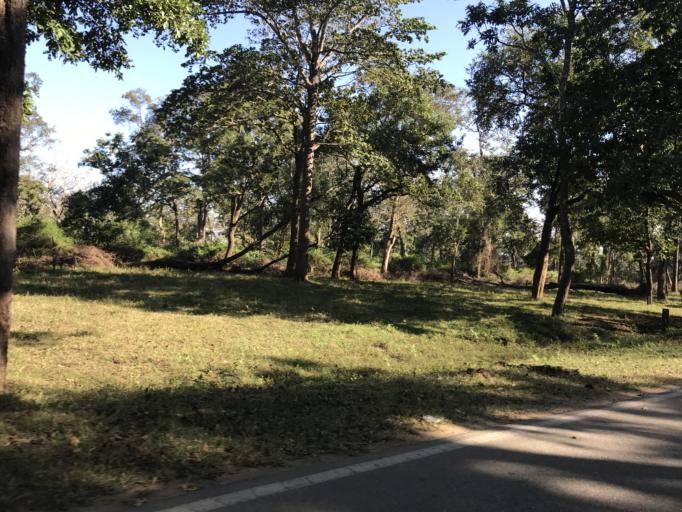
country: IN
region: Karnataka
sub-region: Mysore
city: Heggadadevankote
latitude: 11.9494
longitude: 76.2291
